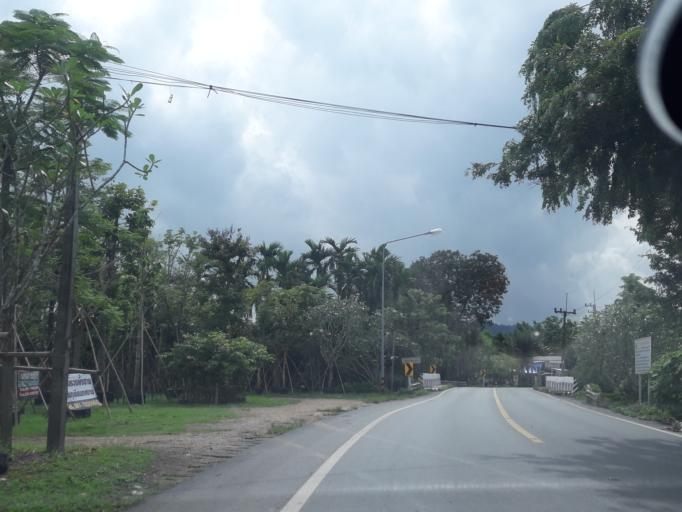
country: TH
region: Sara Buri
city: Wihan Daeng
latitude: 14.4077
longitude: 101.1032
